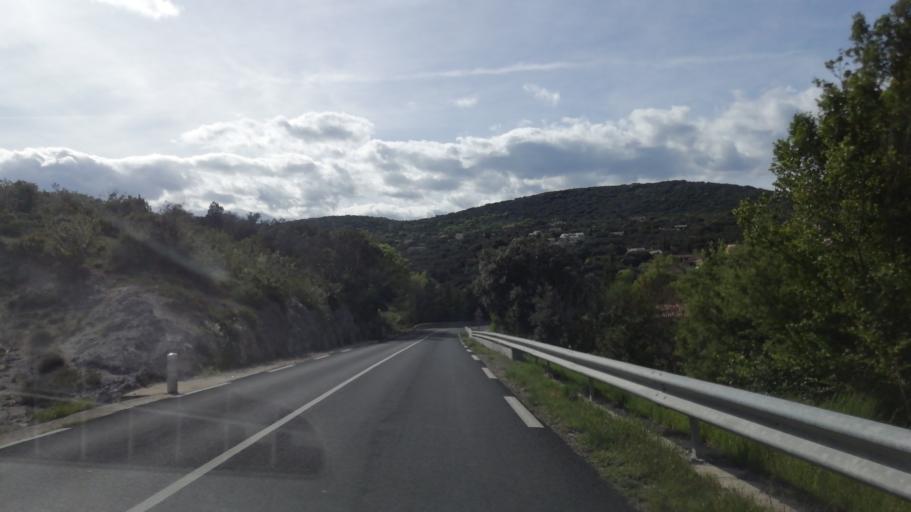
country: FR
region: Languedoc-Roussillon
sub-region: Departement de l'Herault
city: Saint-Martin-de-Londres
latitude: 43.7725
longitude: 3.7223
